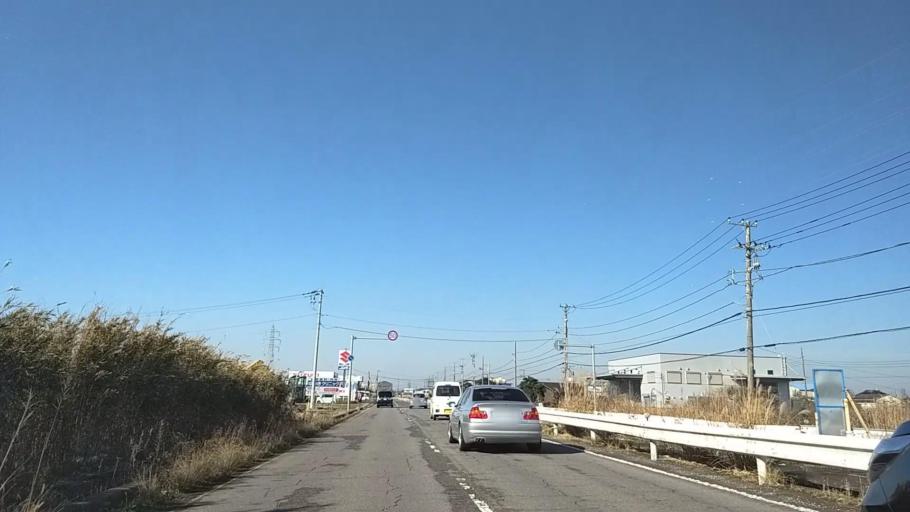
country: JP
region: Chiba
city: Asahi
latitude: 35.7209
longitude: 140.6946
